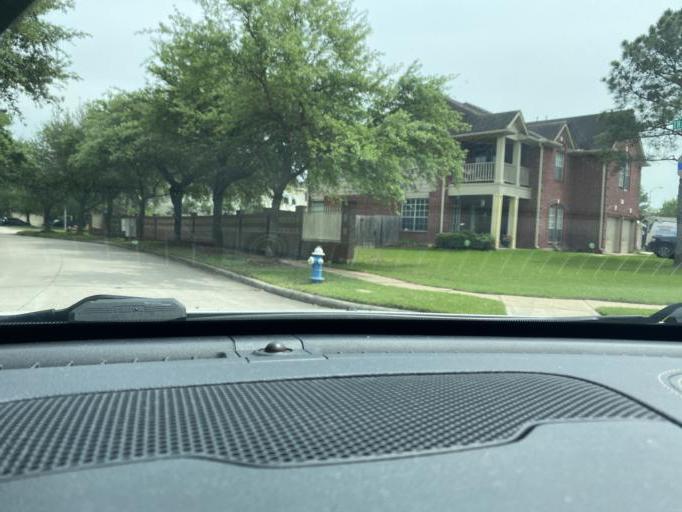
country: US
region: Texas
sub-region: Harris County
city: Jersey Village
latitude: 29.9183
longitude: -95.5817
